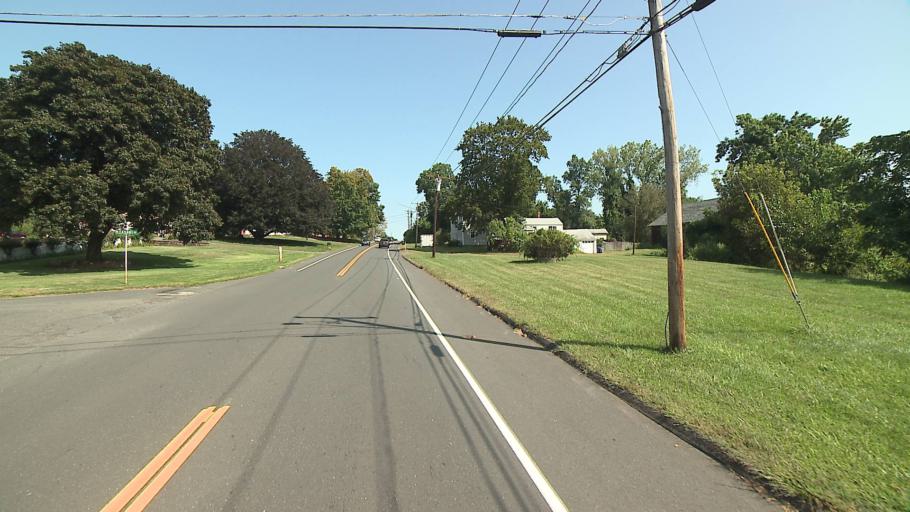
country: US
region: Connecticut
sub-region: Hartford County
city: Windsor Locks
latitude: 41.9392
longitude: -72.6036
